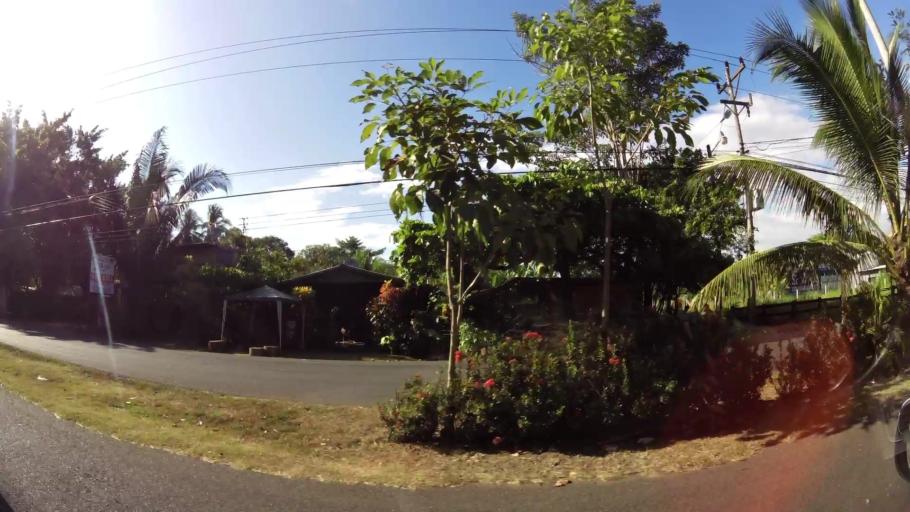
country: CR
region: Puntarenas
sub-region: Canton de Garabito
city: Jaco
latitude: 9.6236
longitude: -84.6365
